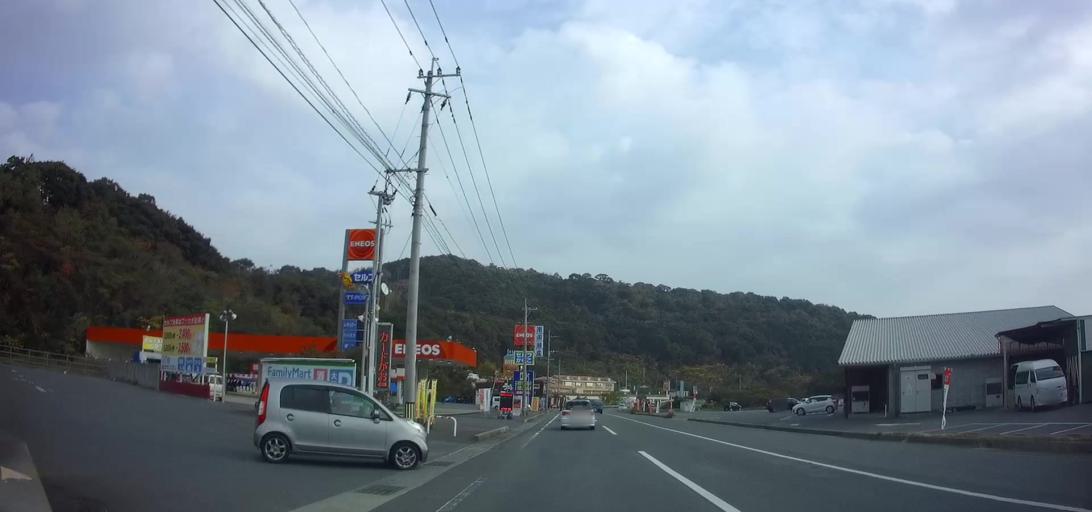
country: JP
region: Nagasaki
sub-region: Isahaya-shi
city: Isahaya
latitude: 32.7943
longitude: 130.1149
